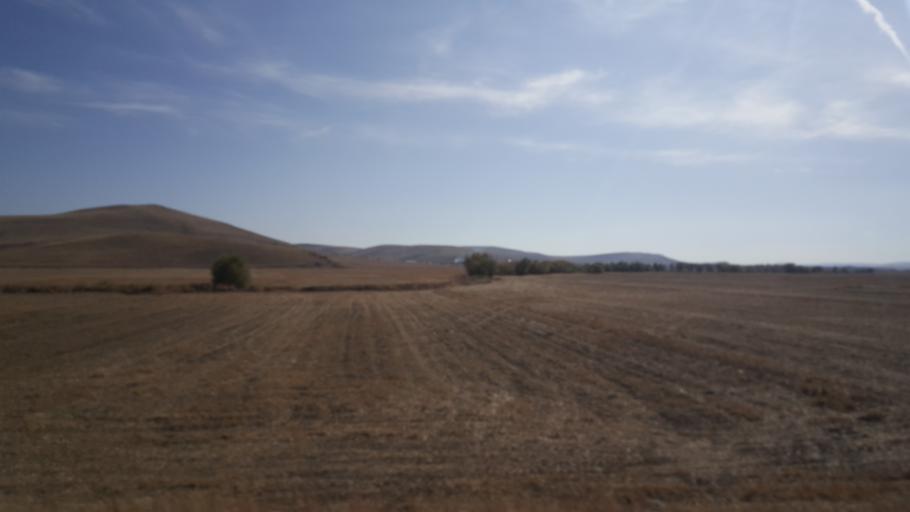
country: TR
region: Ankara
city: Yenice
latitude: 39.3828
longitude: 32.8145
